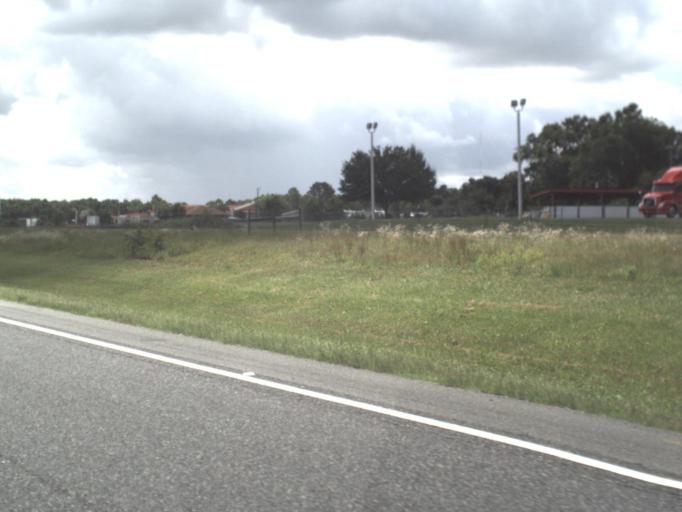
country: US
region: Florida
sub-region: Columbia County
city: Lake City
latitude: 30.1207
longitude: -82.6577
